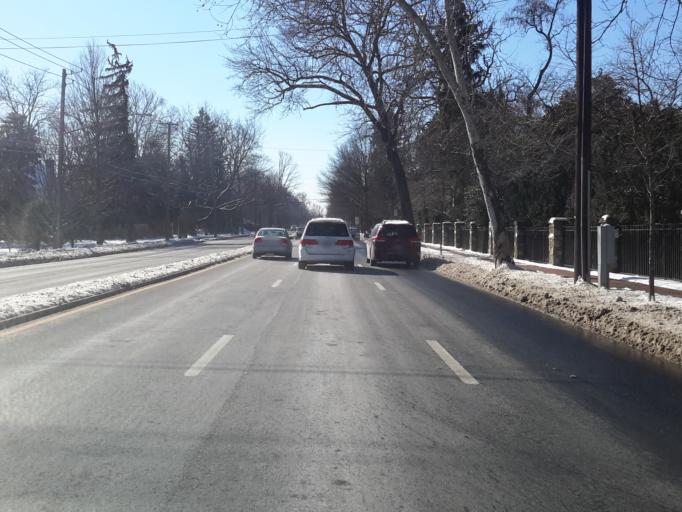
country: US
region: Maryland
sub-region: Montgomery County
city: Chevy Chase
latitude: 38.9735
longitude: -77.0772
